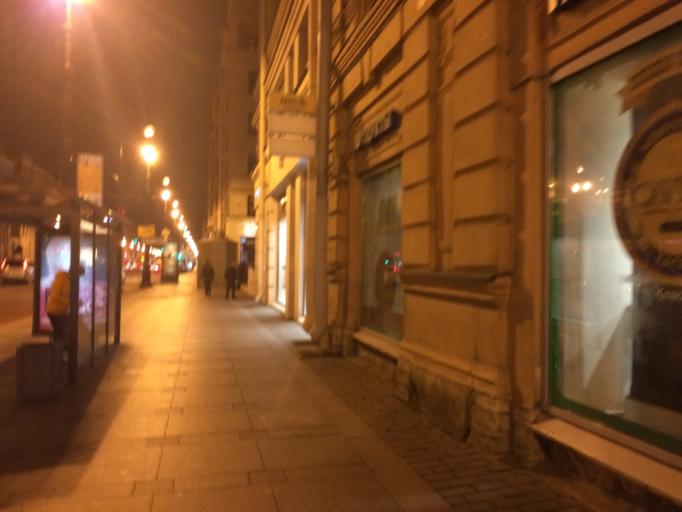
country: RU
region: St.-Petersburg
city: Centralniy
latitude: 59.9264
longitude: 30.3771
